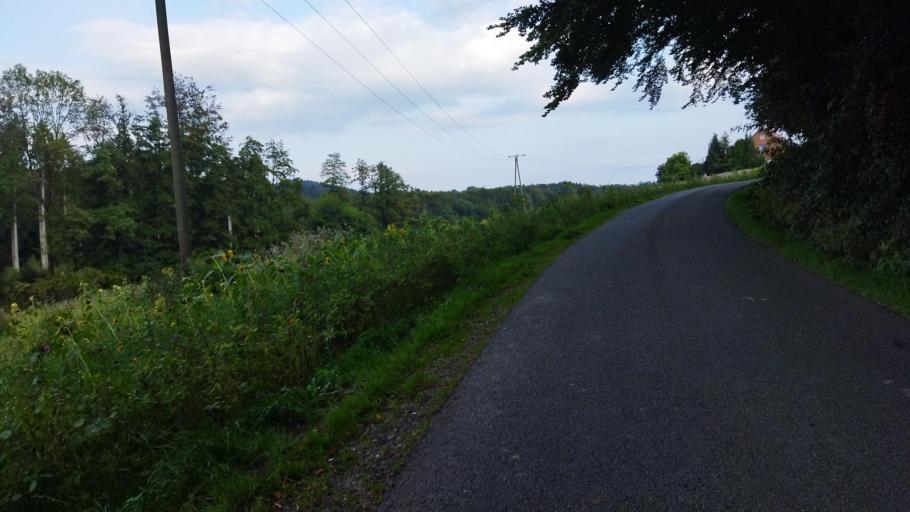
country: DE
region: Lower Saxony
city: Hagen
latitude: 52.1774
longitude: 8.0093
